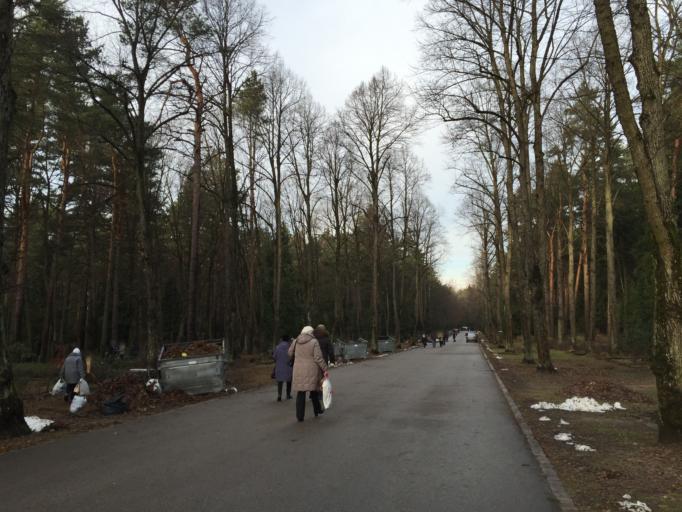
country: LV
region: Riga
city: Jaunciems
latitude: 56.9891
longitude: 24.1463
